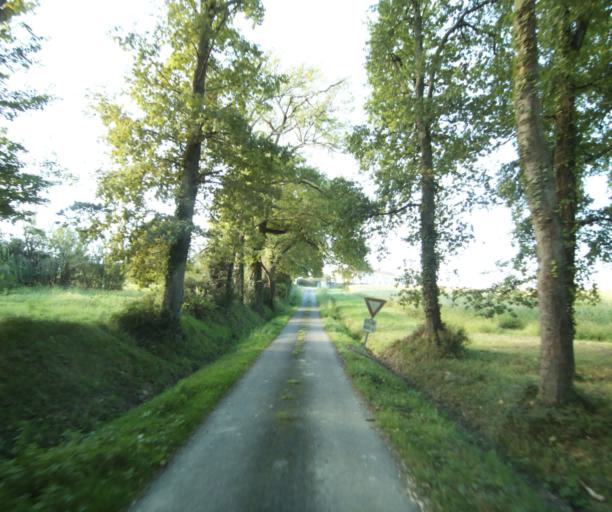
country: FR
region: Midi-Pyrenees
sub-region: Departement du Gers
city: Cazaubon
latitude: 43.8935
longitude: -0.0033
